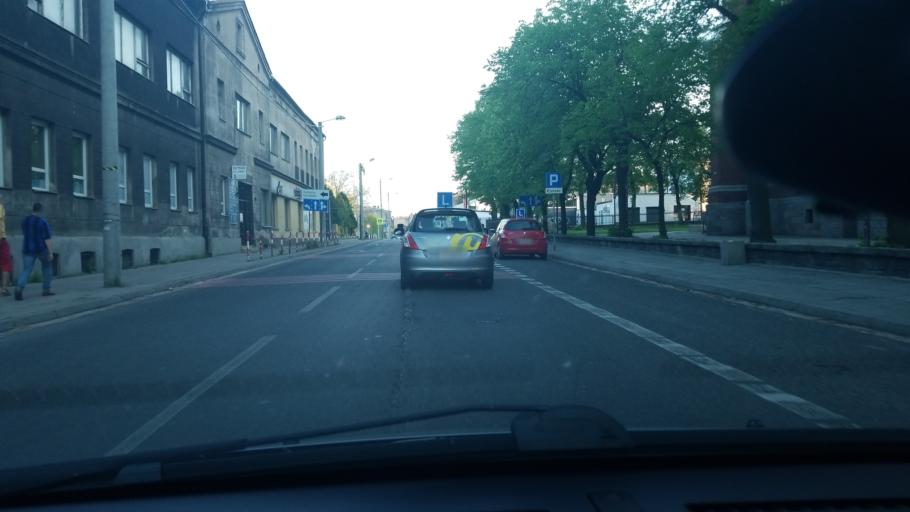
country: PL
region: Silesian Voivodeship
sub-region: Czestochowa
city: Czestochowa
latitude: 50.8087
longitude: 19.1277
